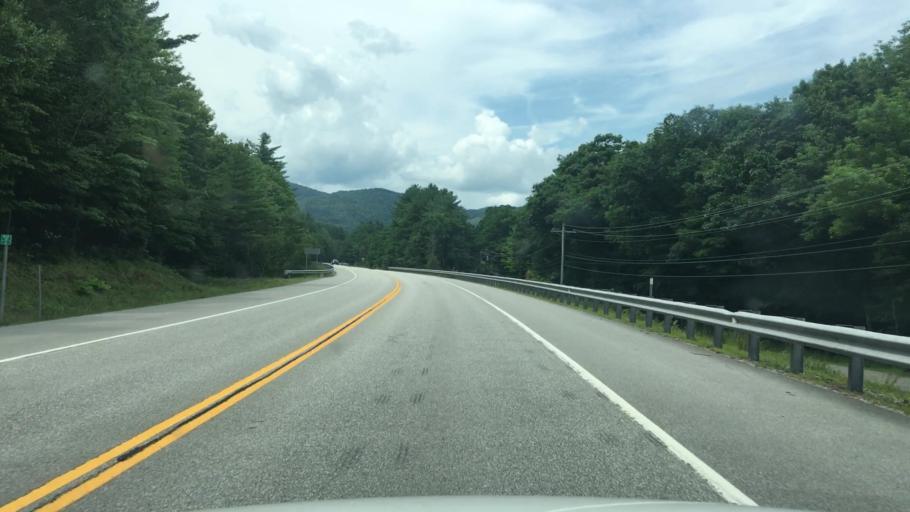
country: US
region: New Hampshire
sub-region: Grafton County
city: Rumney
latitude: 43.7955
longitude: -71.8232
